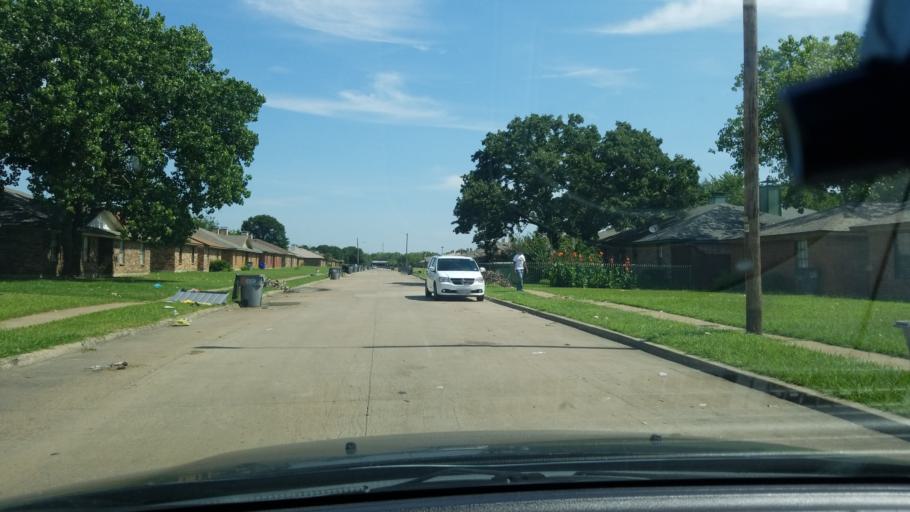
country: US
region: Texas
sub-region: Dallas County
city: Balch Springs
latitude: 32.7285
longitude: -96.6351
